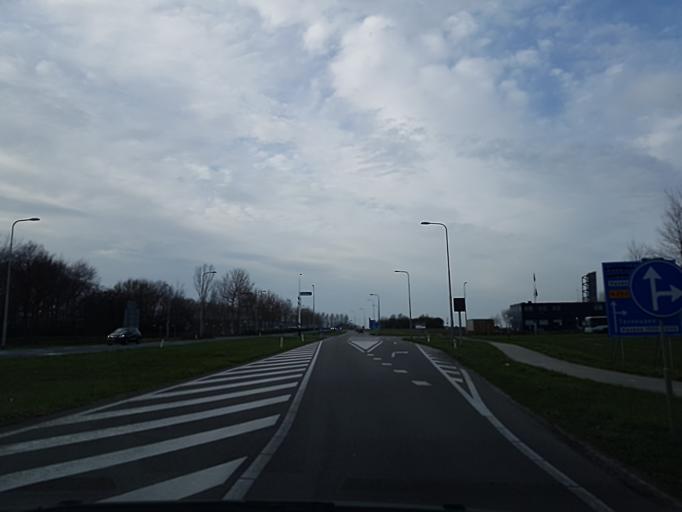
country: NL
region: Zeeland
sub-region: Gemeente Terneuzen
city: Terneuzen
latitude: 51.3251
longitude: 3.8165
